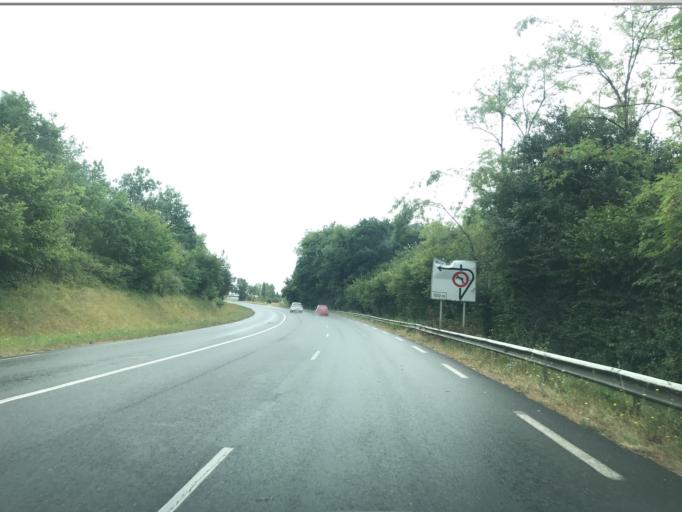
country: FR
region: Aquitaine
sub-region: Departement de la Dordogne
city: Brantome
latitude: 45.3373
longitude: 0.6494
